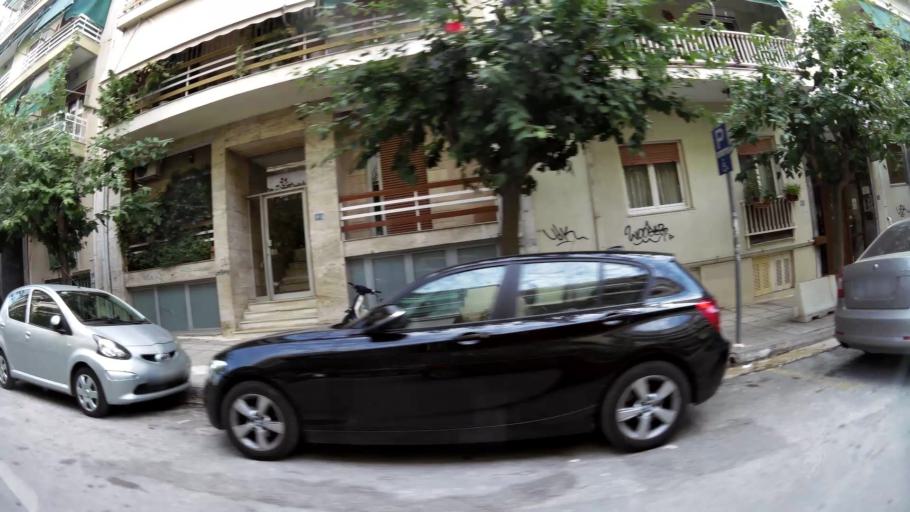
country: GR
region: Attica
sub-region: Nomarchia Athinas
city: Nea Smyrni
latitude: 37.9544
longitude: 23.7171
